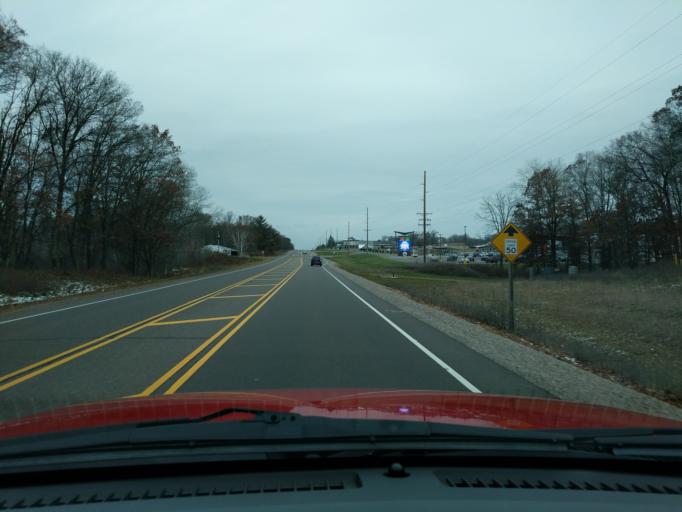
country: US
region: Wisconsin
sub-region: Burnett County
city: Siren
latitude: 45.8088
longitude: -92.1974
